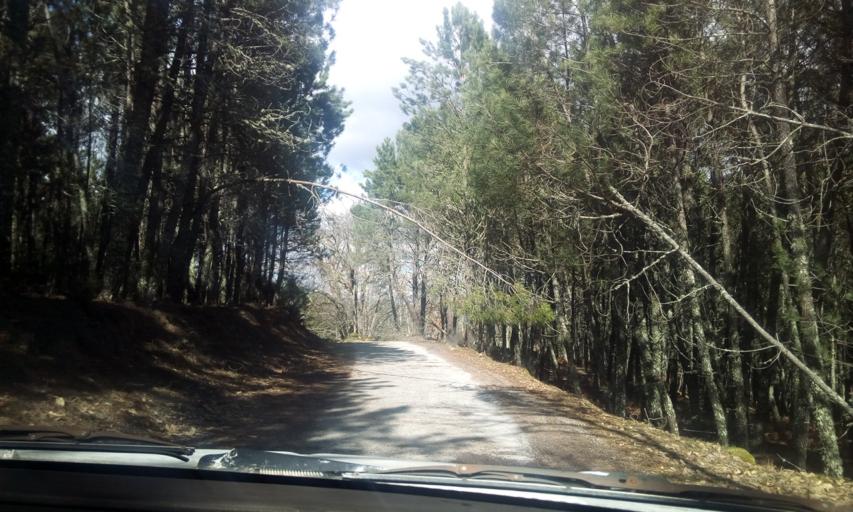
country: PT
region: Guarda
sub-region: Fornos de Algodres
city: Fornos de Algodres
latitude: 40.6500
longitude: -7.5138
